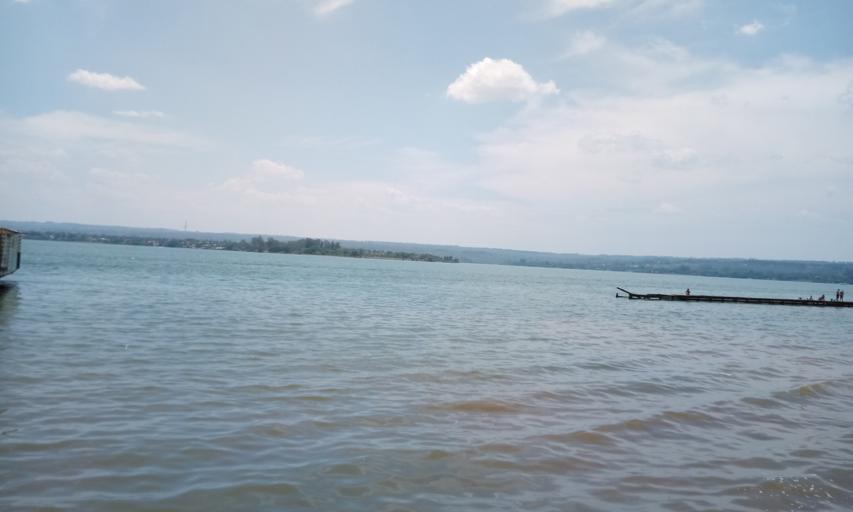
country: BR
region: Federal District
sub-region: Brasilia
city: Brasilia
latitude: -15.7858
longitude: -47.8378
